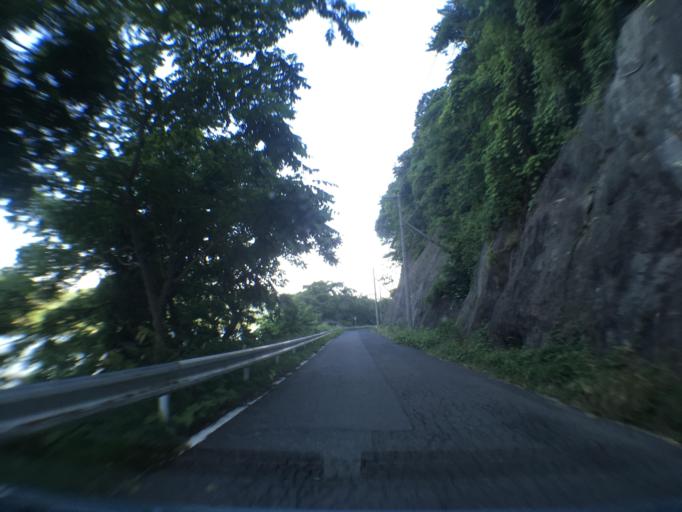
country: JP
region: Miyagi
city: Wakuya
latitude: 38.6297
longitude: 141.2884
